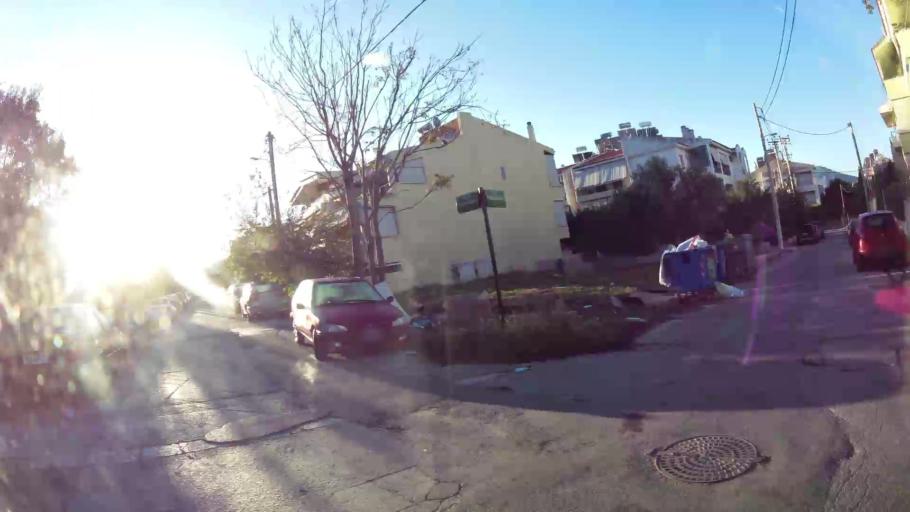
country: GR
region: Attica
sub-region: Nomarchia Anatolikis Attikis
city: Gerakas
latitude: 38.0334
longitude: 23.8534
